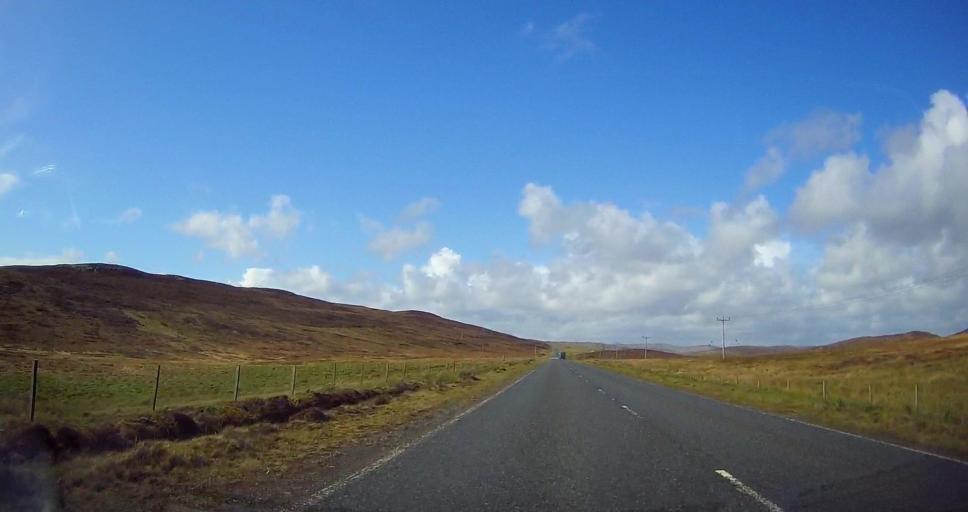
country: GB
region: Scotland
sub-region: Shetland Islands
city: Lerwick
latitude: 60.2070
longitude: -1.2333
